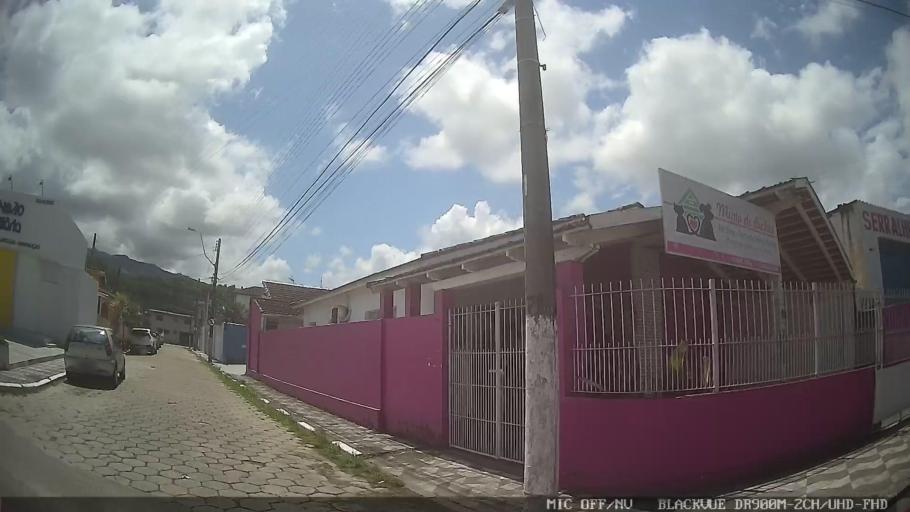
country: BR
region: Sao Paulo
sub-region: Caraguatatuba
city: Caraguatatuba
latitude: -23.6231
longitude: -45.4173
